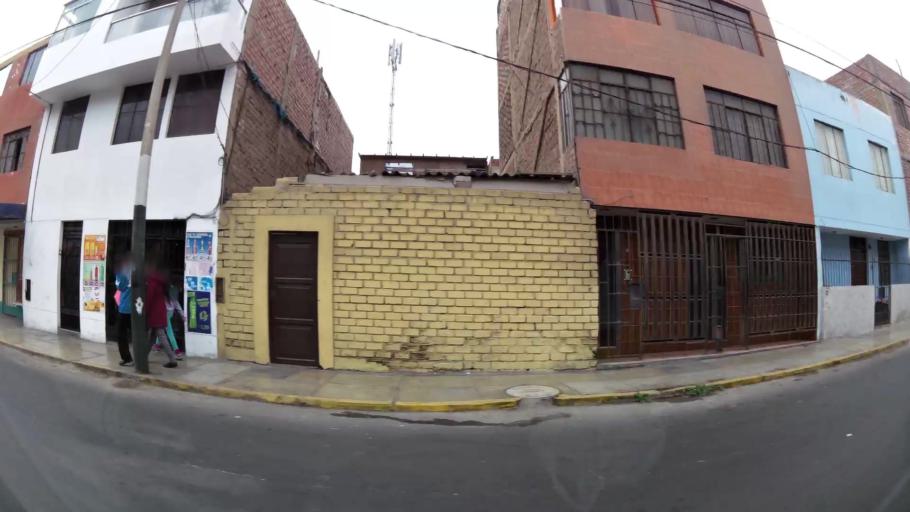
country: PE
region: Callao
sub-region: Callao
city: Callao
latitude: -12.0635
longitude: -77.1270
